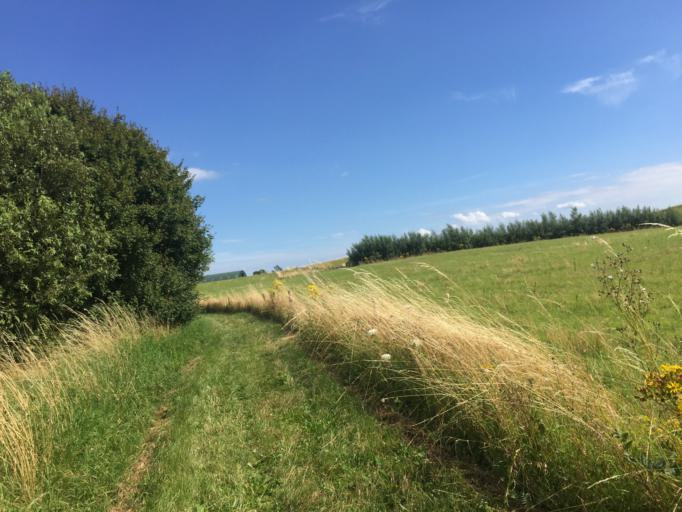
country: DK
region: South Denmark
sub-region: Faaborg-Midtfyn Kommune
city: Faaborg
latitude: 55.0662
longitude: 10.2384
